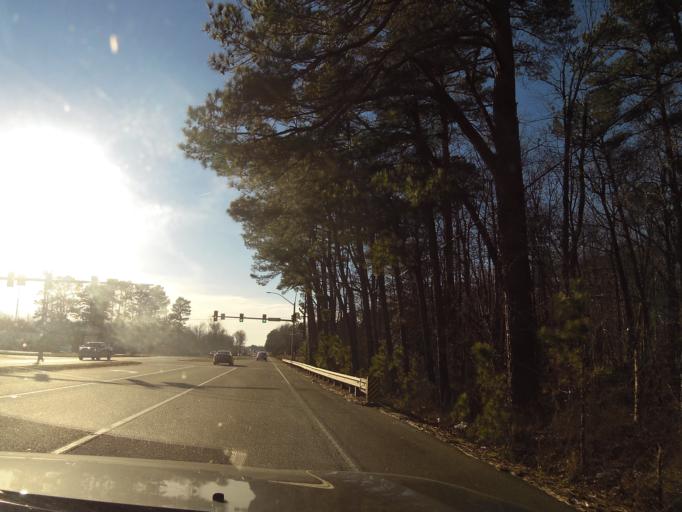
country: US
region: Virginia
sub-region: Isle of Wight County
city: Windsor
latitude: 36.6915
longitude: -76.7439
